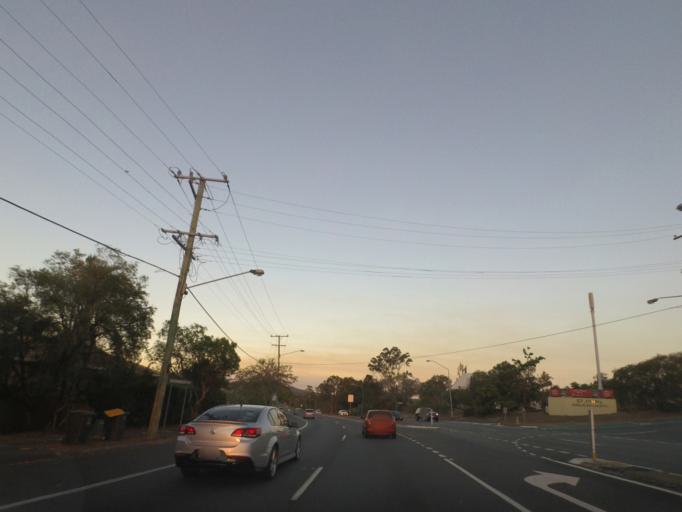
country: AU
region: Queensland
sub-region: Brisbane
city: Mansfield
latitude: -27.5546
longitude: 153.0994
